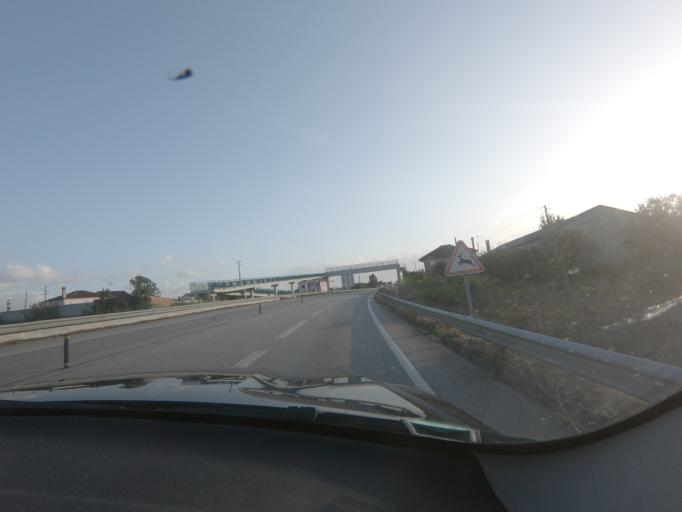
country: PT
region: Viseu
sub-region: Santa Comba Dao
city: Santa Comba Dao
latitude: 40.3767
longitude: -8.1211
